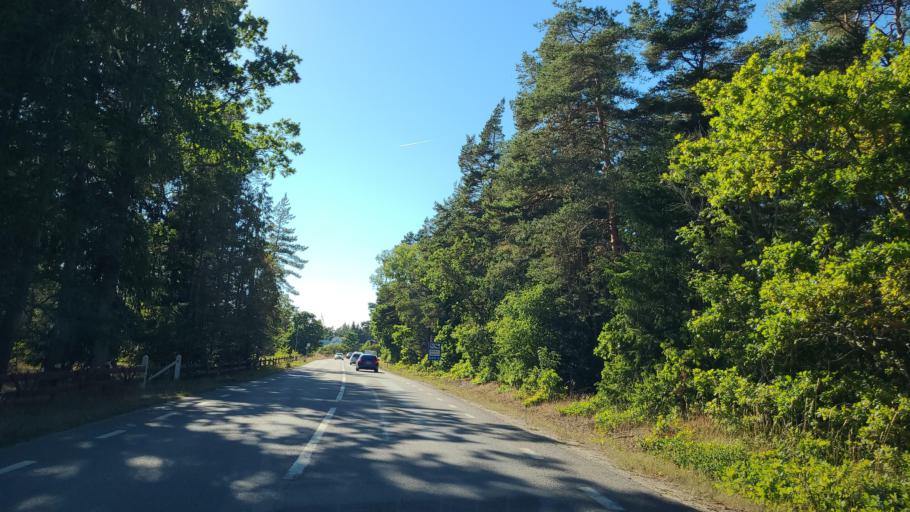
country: SE
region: Kalmar
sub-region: Borgholms Kommun
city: Borgholm
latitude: 57.2589
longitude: 17.0430
